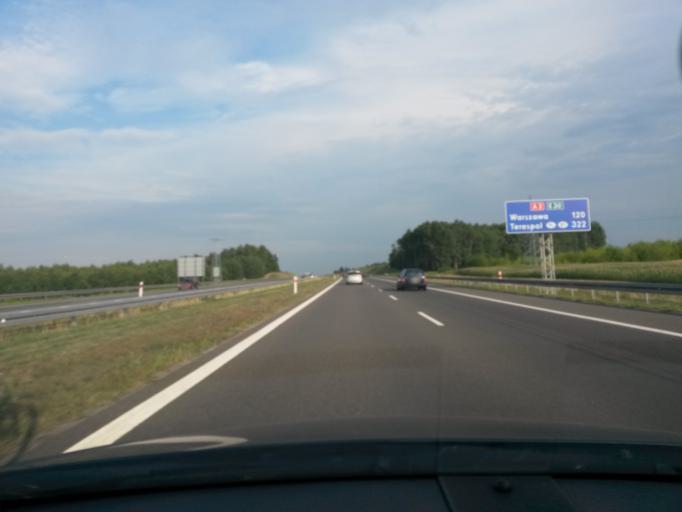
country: PL
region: Lodz Voivodeship
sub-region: Powiat zgierski
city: Zgierz
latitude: 51.9057
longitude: 19.4493
